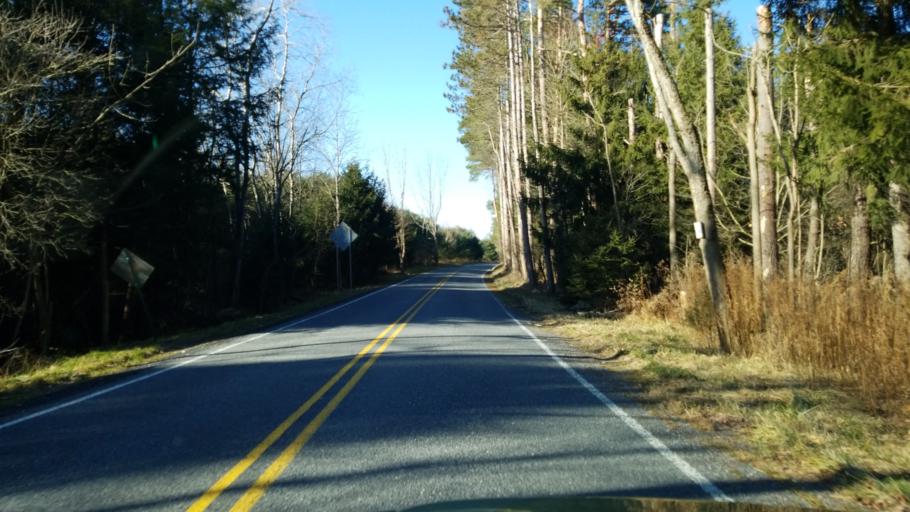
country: US
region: Pennsylvania
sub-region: Clearfield County
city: Hyde
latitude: 40.9757
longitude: -78.4614
